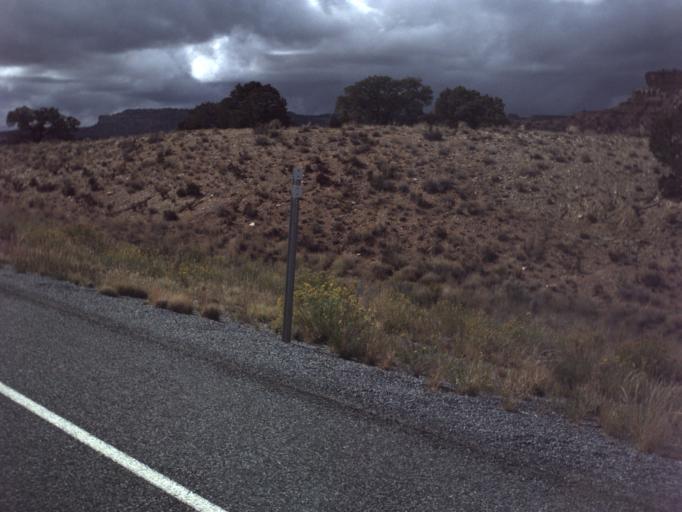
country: US
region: Utah
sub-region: Emery County
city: Castle Dale
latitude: 38.8839
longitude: -110.6551
